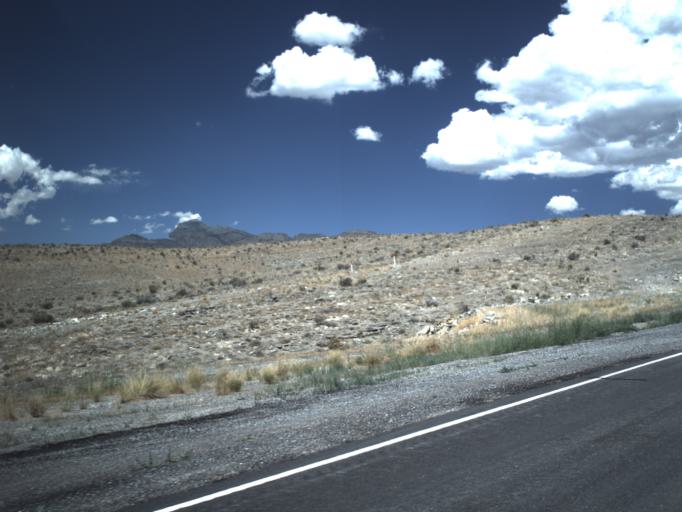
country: US
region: Utah
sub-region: Beaver County
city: Milford
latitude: 39.0313
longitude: -113.3423
